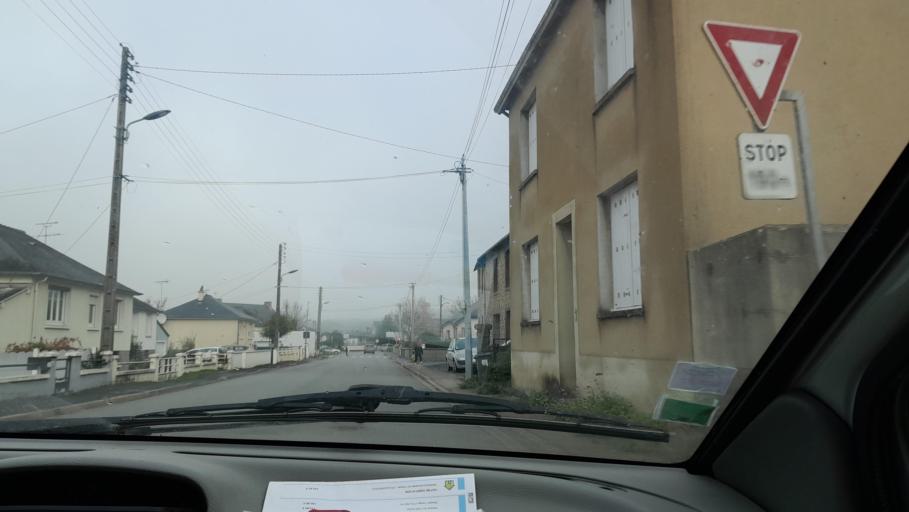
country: FR
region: Pays de la Loire
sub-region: Departement de la Mayenne
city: Saint-Pierre-la-Cour
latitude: 48.1117
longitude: -1.0249
